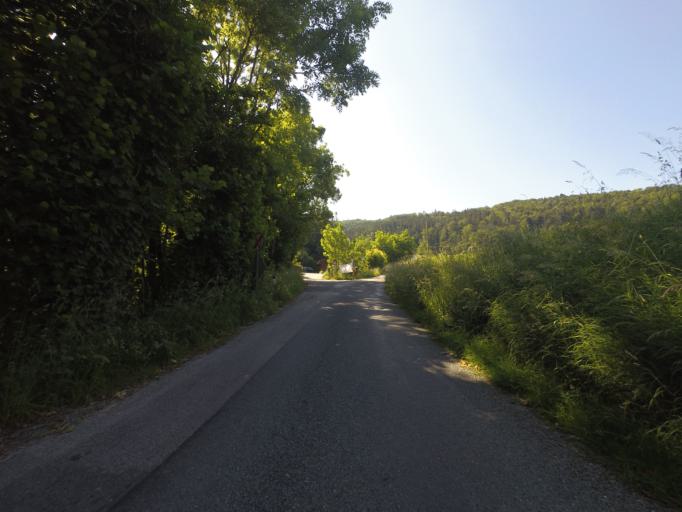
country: AT
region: Salzburg
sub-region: Politischer Bezirk Salzburg-Umgebung
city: Elsbethen
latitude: 47.7619
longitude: 13.1050
